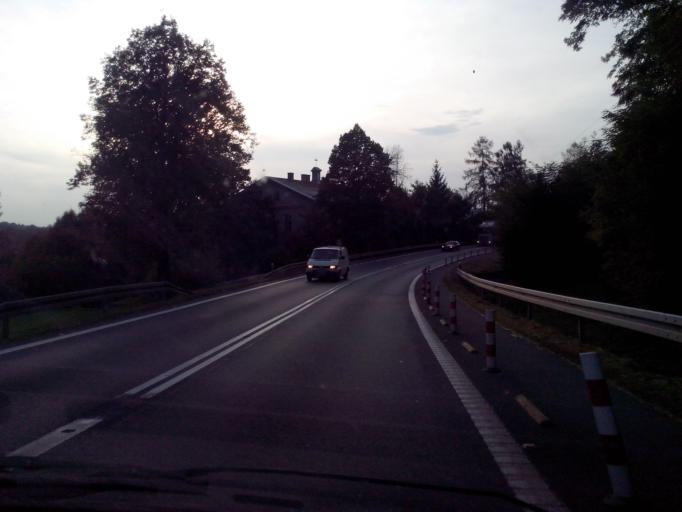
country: PL
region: Subcarpathian Voivodeship
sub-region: Powiat strzyzowski
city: Jawornik
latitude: 49.8052
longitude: 21.8956
